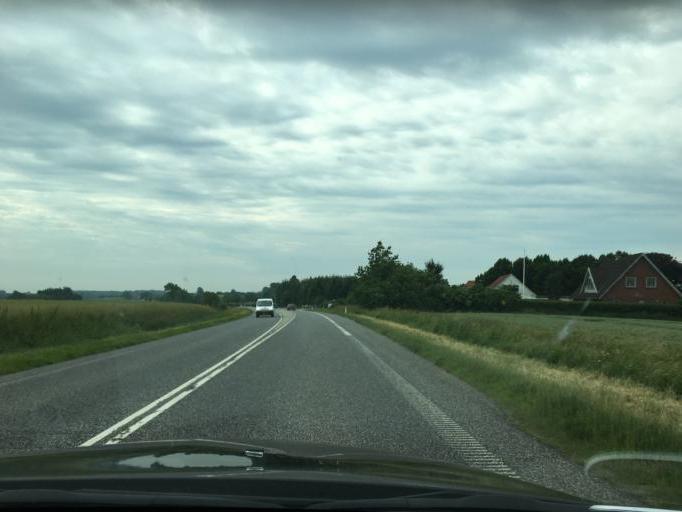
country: DK
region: South Denmark
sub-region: Kolding Kommune
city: Kolding
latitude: 55.5919
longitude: 9.4932
